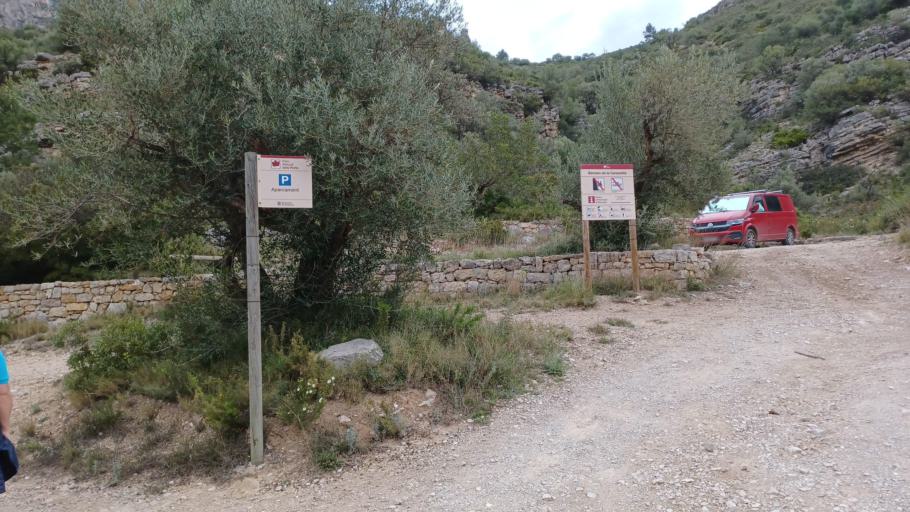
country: ES
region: Catalonia
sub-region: Provincia de Tarragona
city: Mas de Barberans
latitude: 40.8068
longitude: 0.3924
